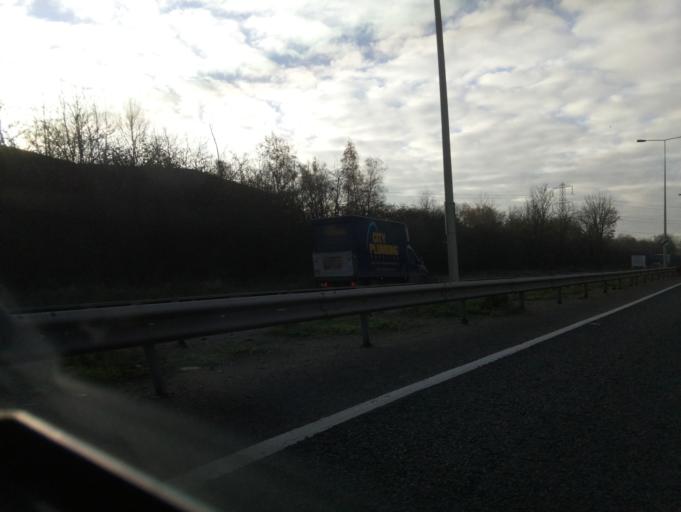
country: GB
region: England
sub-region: Staffordshire
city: Barton under Needwood
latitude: 52.7580
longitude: -1.7069
